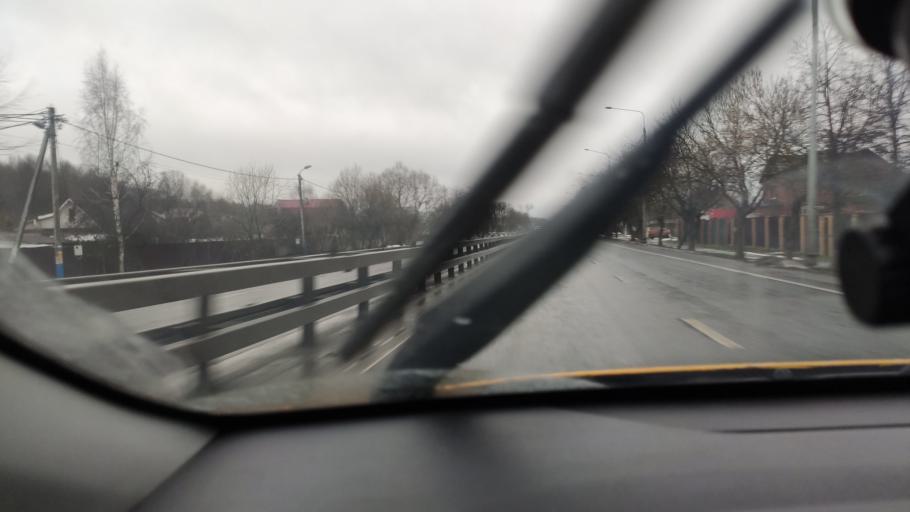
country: RU
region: Moskovskaya
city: Troitsk
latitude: 55.3272
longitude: 37.2737
